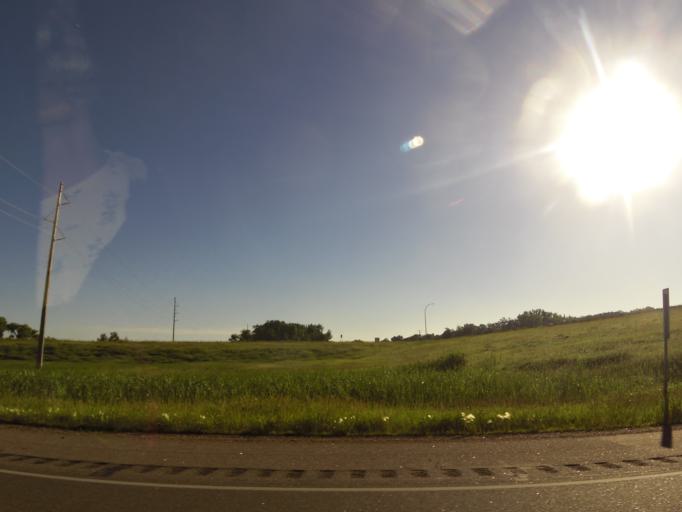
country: US
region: Minnesota
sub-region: Stearns County
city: Saint Joseph
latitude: 45.5158
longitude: -94.2850
